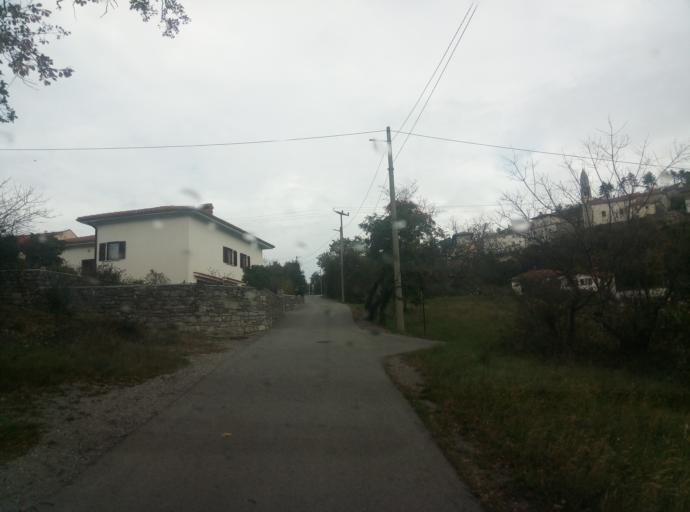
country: SI
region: Ajdovscina
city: Lokavec
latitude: 45.8213
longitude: 13.8452
